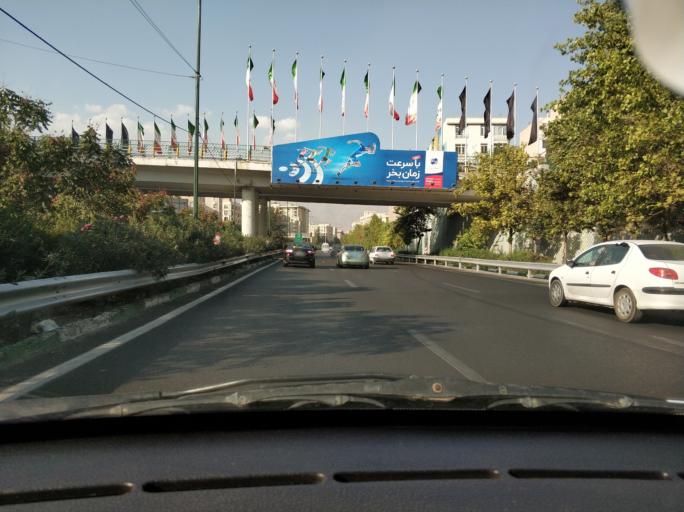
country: IR
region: Tehran
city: Tajrish
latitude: 35.7603
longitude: 51.4659
